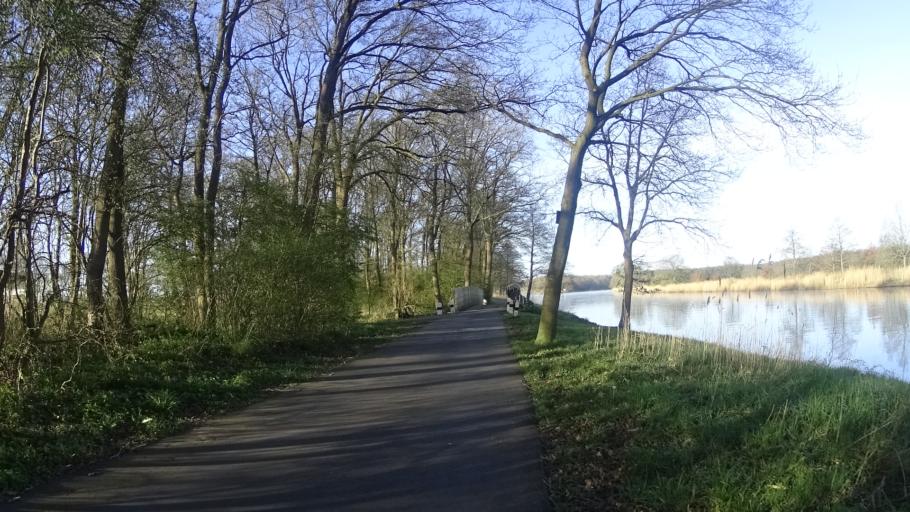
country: DE
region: Lower Saxony
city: Niederlangen
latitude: 52.8409
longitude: 7.2880
